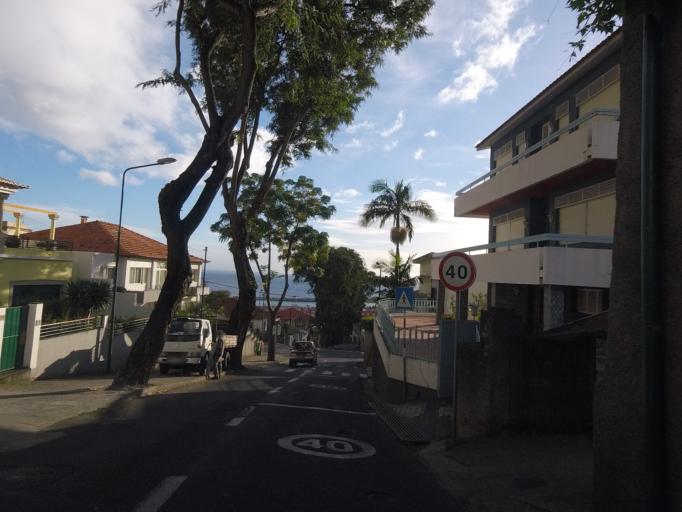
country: PT
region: Madeira
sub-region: Funchal
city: Nossa Senhora do Monte
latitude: 32.6585
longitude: -16.9032
